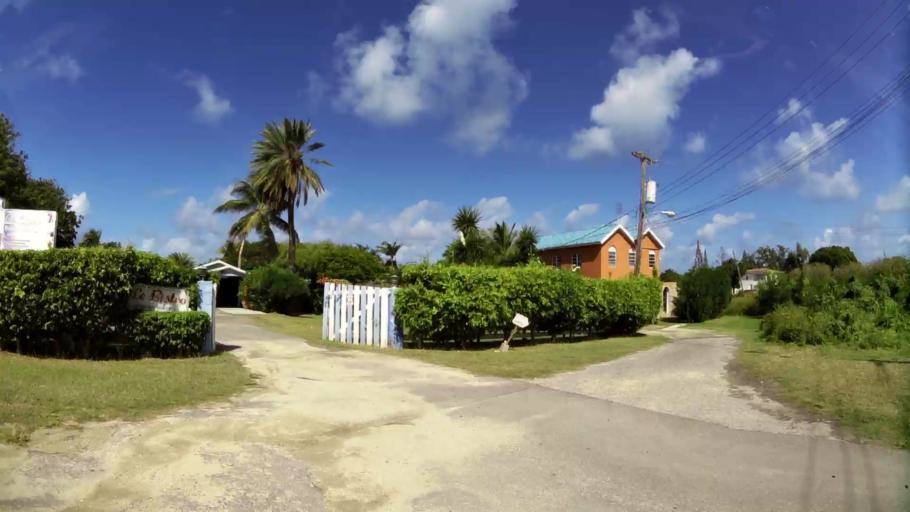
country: AG
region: Saint George
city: Piggotts
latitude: 17.1670
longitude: -61.8031
